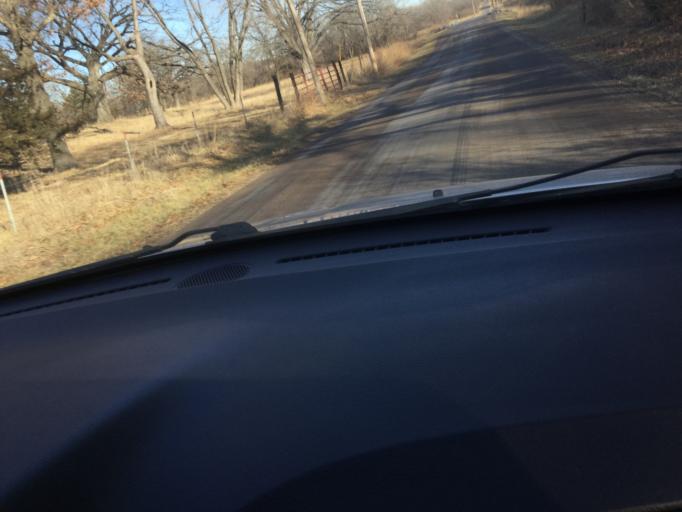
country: US
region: Kansas
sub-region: Shawnee County
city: Topeka
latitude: 39.1165
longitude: -95.7040
